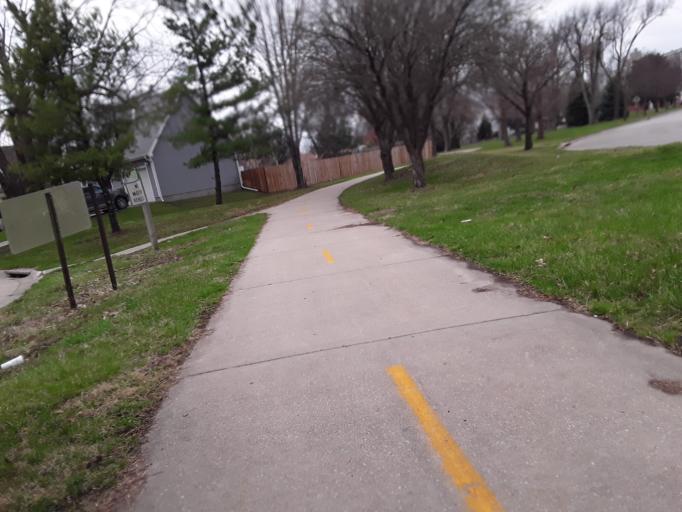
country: US
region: Nebraska
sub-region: Lancaster County
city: Lincoln
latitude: 40.8404
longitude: -96.6705
